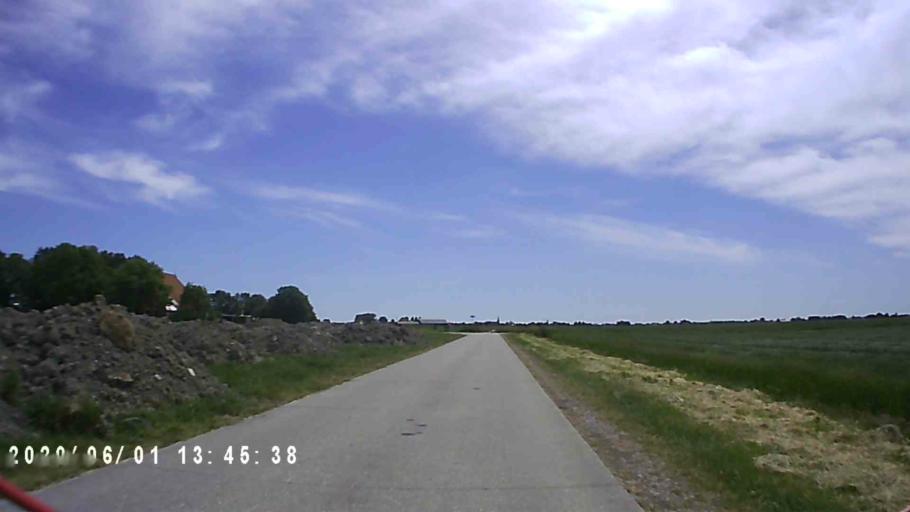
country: NL
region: Friesland
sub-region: Gemeente Littenseradiel
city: Wommels
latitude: 53.0916
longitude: 5.6227
